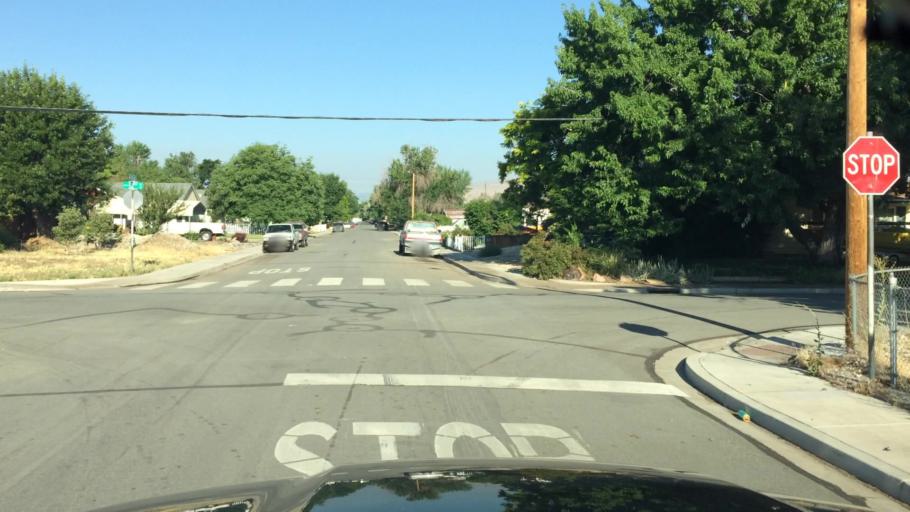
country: US
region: Nevada
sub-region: Washoe County
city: Sparks
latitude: 39.5460
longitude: -119.7586
